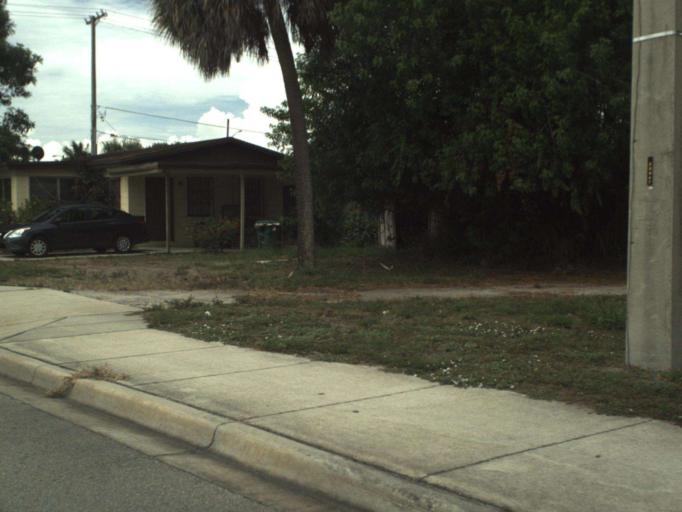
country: US
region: Florida
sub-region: Saint Lucie County
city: Fort Pierce North
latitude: 27.4663
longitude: -80.3498
